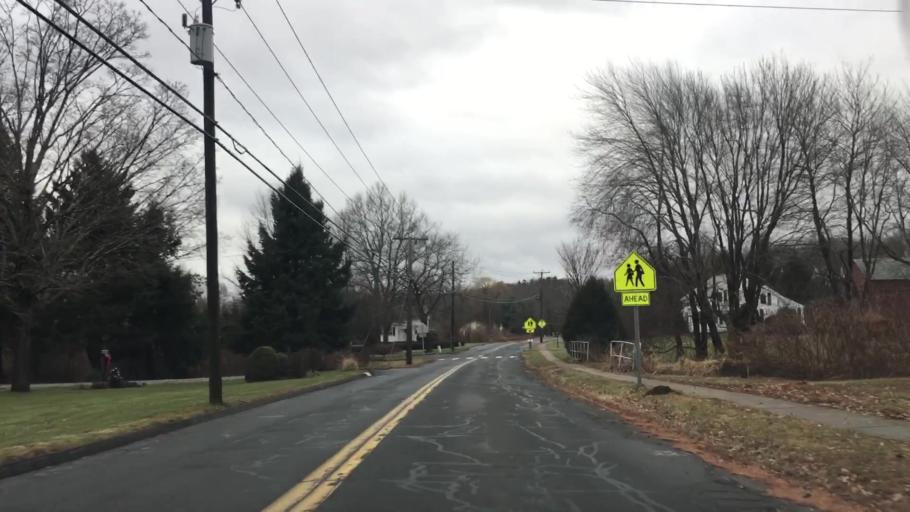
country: US
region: Connecticut
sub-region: Tolland County
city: Rockville
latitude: 41.8438
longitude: -72.5104
